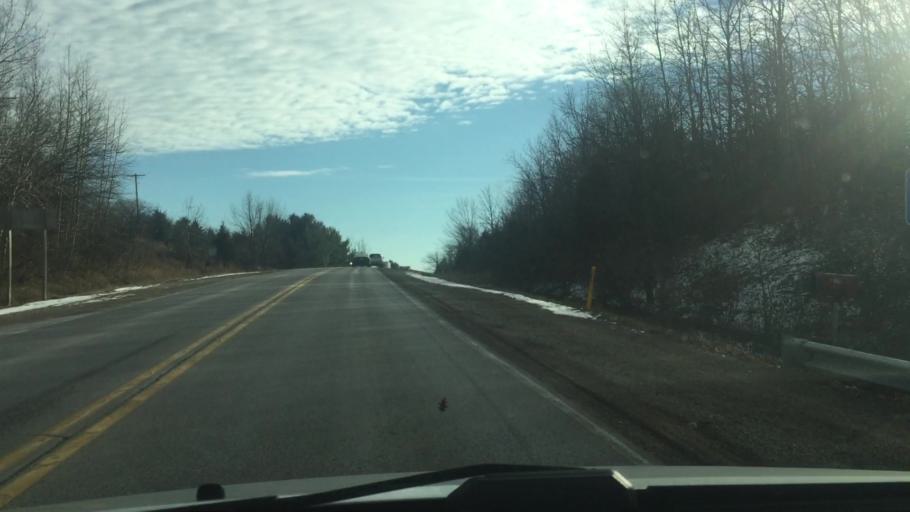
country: US
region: Wisconsin
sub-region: Waukesha County
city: Delafield
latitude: 43.0518
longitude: -88.4046
